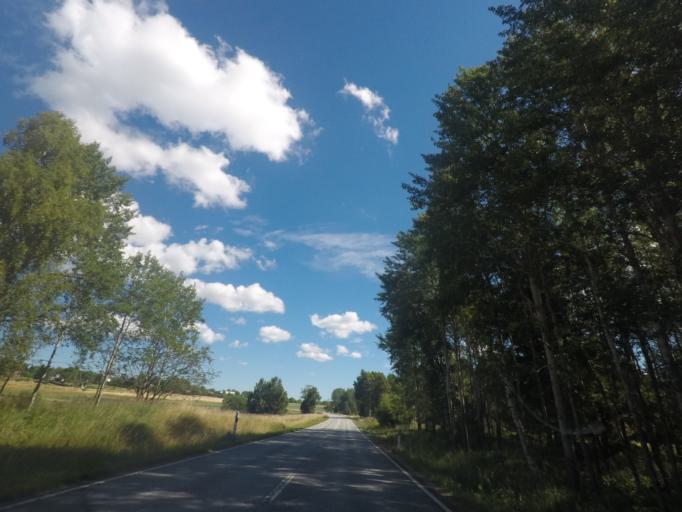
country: SE
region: Stockholm
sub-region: Norrtalje Kommun
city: Hallstavik
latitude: 59.9535
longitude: 18.7752
